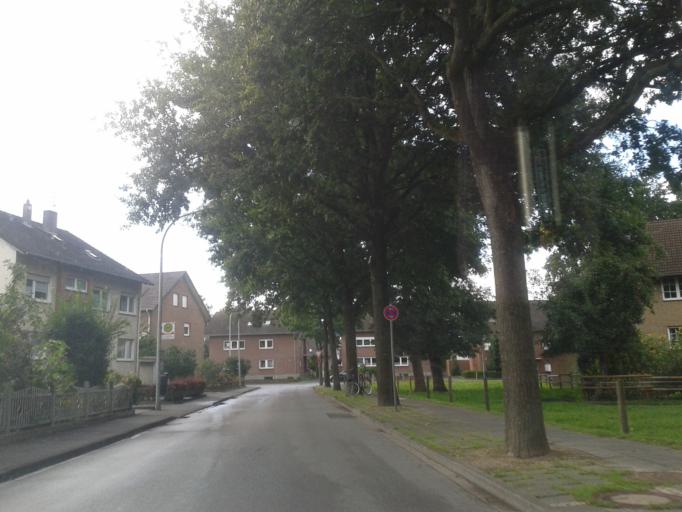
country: DE
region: North Rhine-Westphalia
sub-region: Regierungsbezirk Detmold
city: Hovelhof
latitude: 51.7611
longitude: 8.6654
